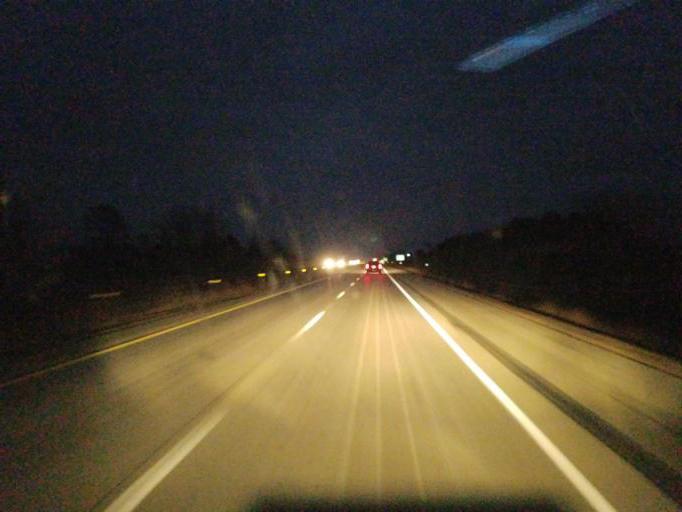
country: US
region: Iowa
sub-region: Guthrie County
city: Stuart
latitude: 41.4958
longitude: -94.4683
